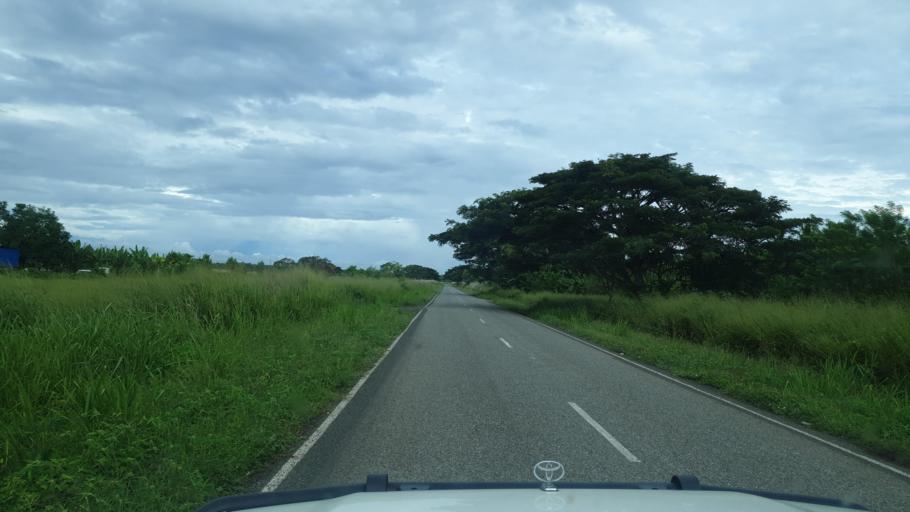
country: PG
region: National Capital
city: Port Moresby
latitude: -9.0161
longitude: 146.8461
